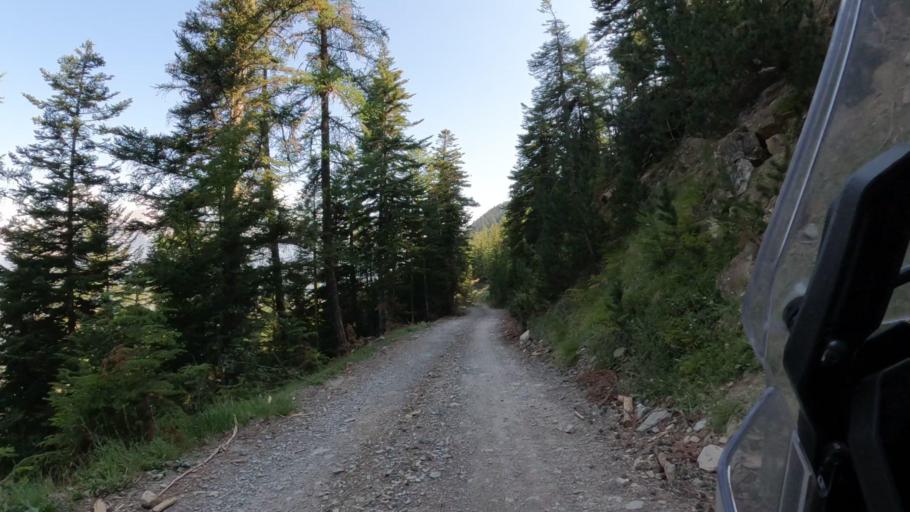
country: FR
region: Provence-Alpes-Cote d'Azur
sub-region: Departement des Hautes-Alpes
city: Embrun
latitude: 44.5889
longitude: 6.5652
